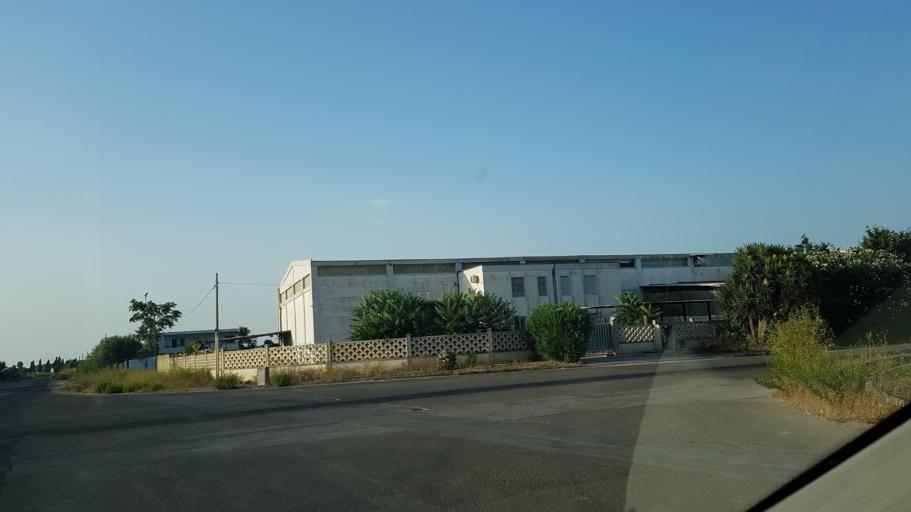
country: IT
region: Apulia
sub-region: Provincia di Brindisi
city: La Rosa
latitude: 40.6280
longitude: 17.9720
